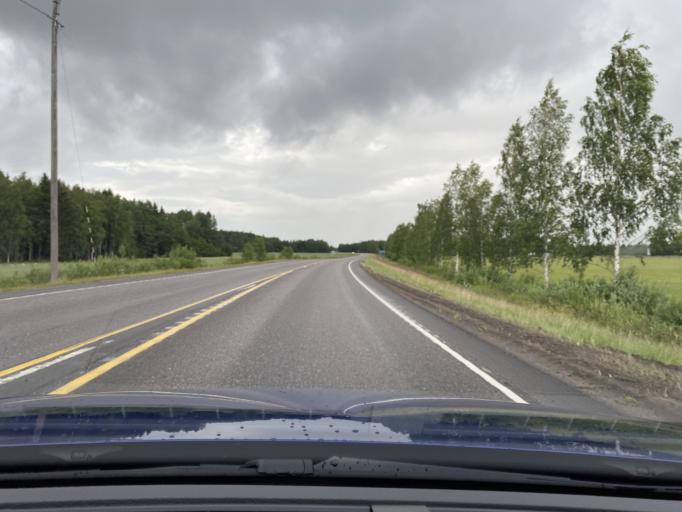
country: FI
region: Uusimaa
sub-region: Helsinki
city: Hyvinge
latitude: 60.5790
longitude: 24.7965
